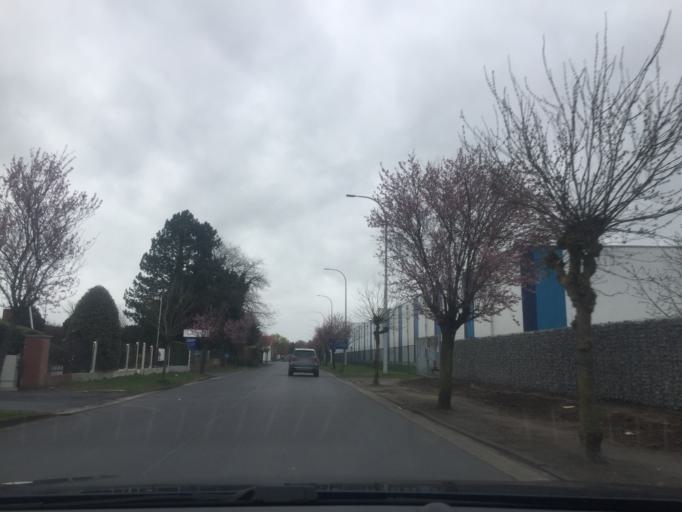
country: BE
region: Flanders
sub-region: Provincie Oost-Vlaanderen
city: Eeklo
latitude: 51.1806
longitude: 3.5483
